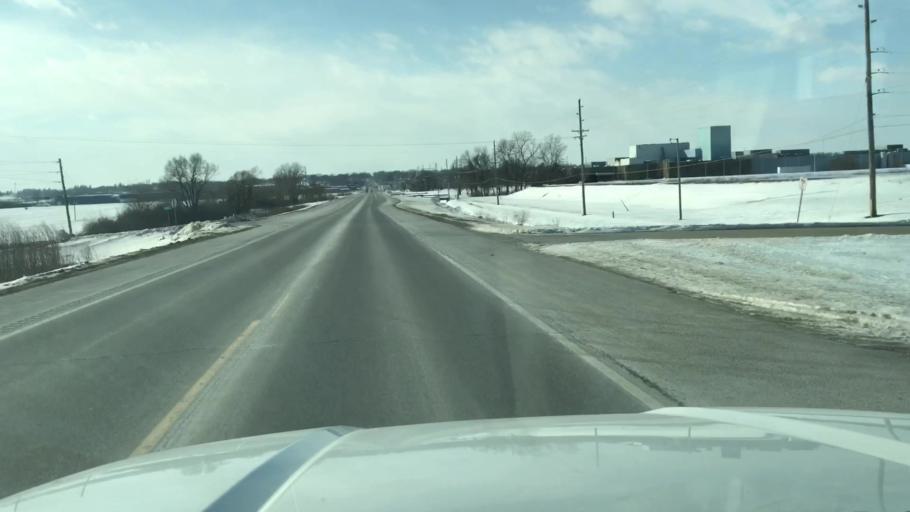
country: US
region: Missouri
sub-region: Nodaway County
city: Maryville
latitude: 40.3450
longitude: -94.8342
